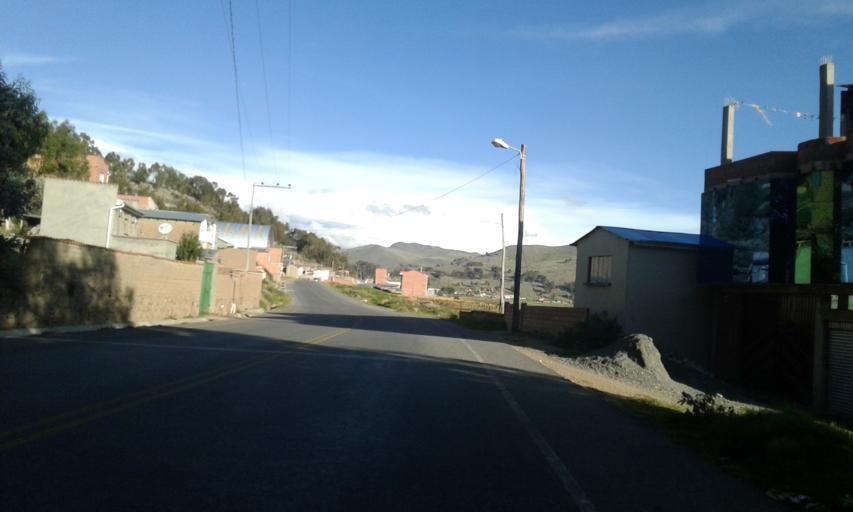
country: BO
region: La Paz
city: Achacachi
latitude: -16.0429
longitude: -68.8337
